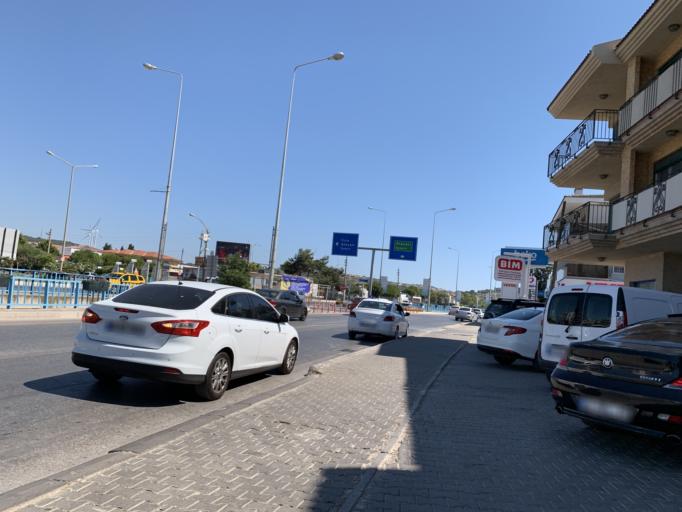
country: TR
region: Izmir
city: Cesme
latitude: 38.3165
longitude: 26.3039
